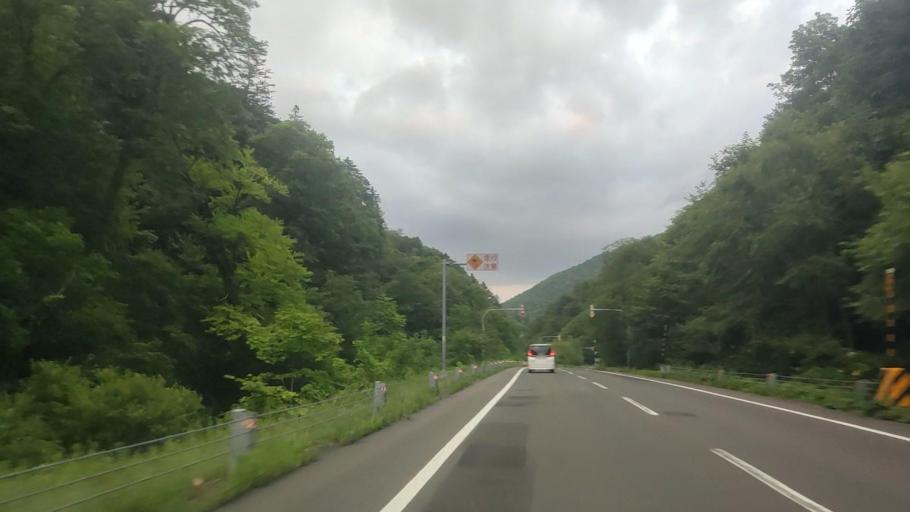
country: JP
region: Hokkaido
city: Shimo-furano
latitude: 43.3430
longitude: 142.2806
